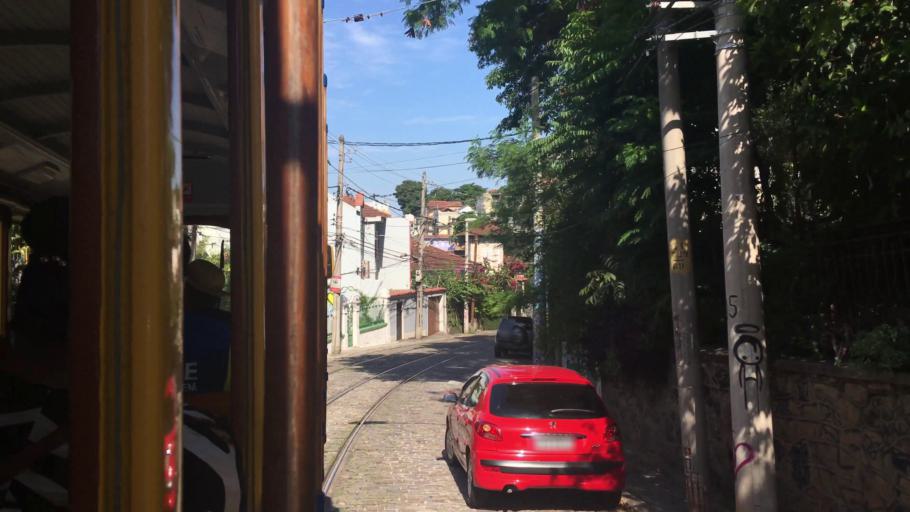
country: BR
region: Rio de Janeiro
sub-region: Rio De Janeiro
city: Rio de Janeiro
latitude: -22.9160
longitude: -43.1835
